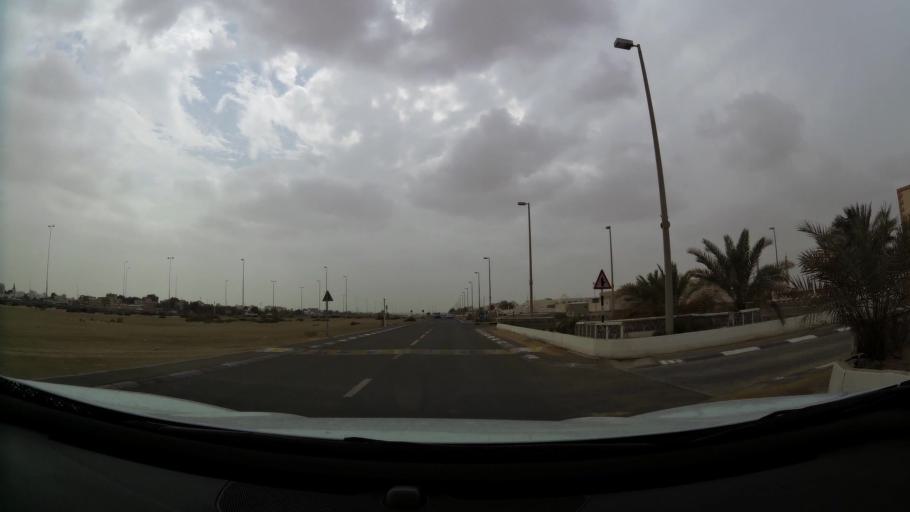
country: AE
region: Abu Dhabi
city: Abu Dhabi
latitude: 24.3520
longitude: 54.6521
